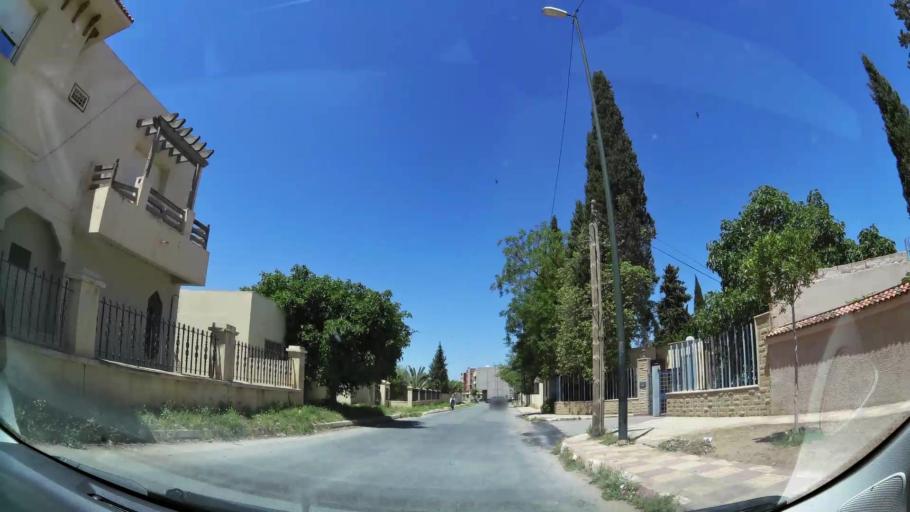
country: MA
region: Oriental
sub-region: Oujda-Angad
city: Oujda
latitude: 34.6682
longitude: -1.8743
